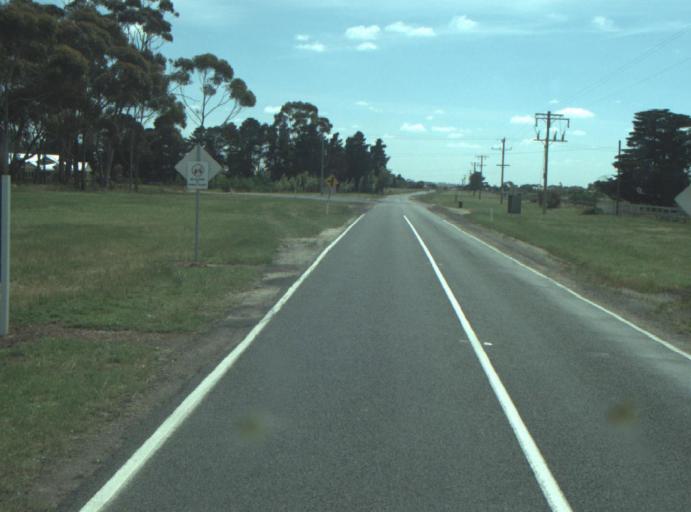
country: AU
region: Victoria
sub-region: Wyndham
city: Little River
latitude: -37.9764
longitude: 144.5094
